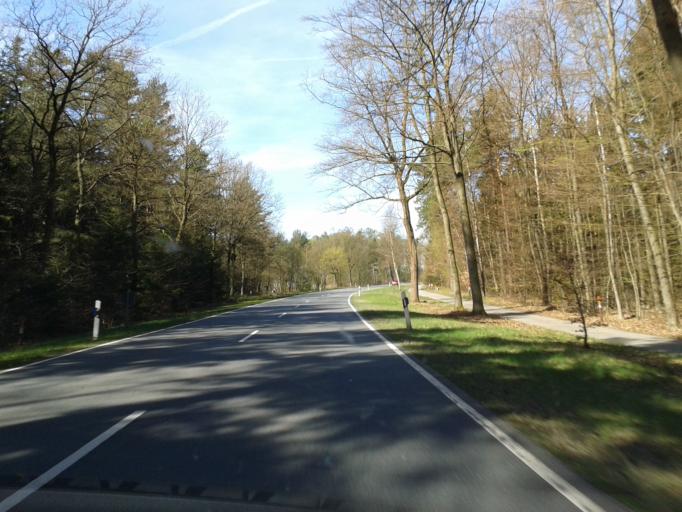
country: DE
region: Lower Saxony
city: Eimke
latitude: 52.9660
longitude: 10.2890
